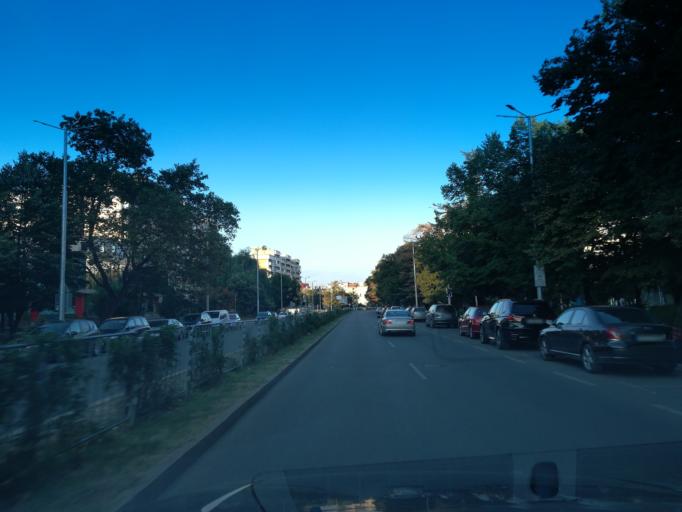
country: BG
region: Plovdiv
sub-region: Obshtina Plovdiv
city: Plovdiv
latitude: 42.1452
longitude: 24.7560
